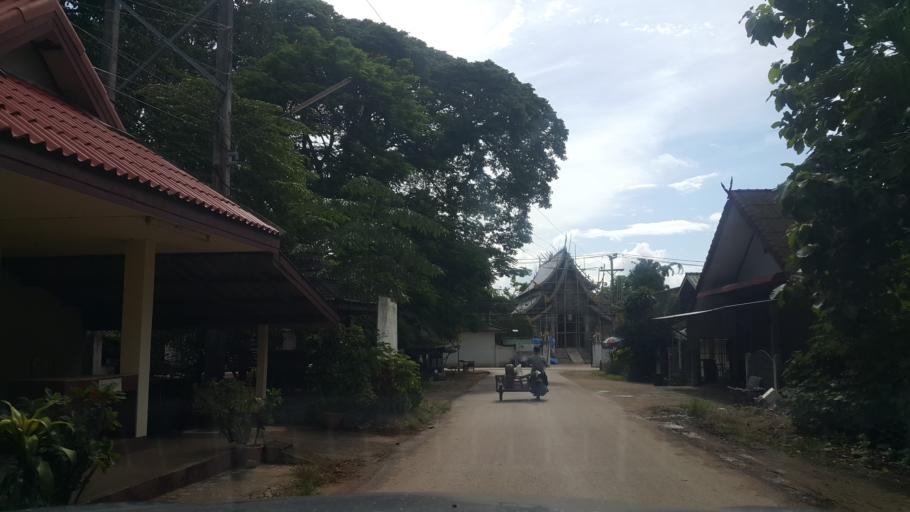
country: TH
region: Chiang Mai
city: Mae Taeng
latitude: 19.1856
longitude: 98.9907
